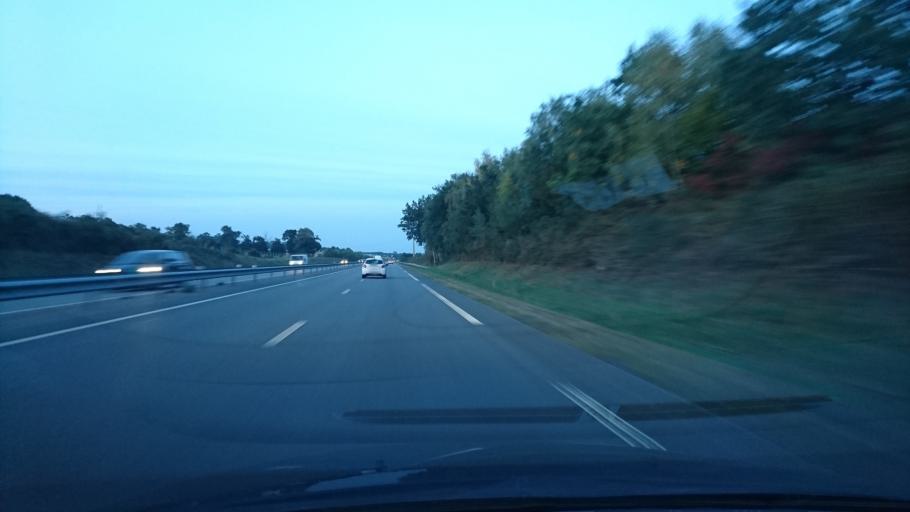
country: FR
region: Brittany
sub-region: Departement d'Ille-et-Vilaine
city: Chavagne
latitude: 48.0159
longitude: -1.7964
